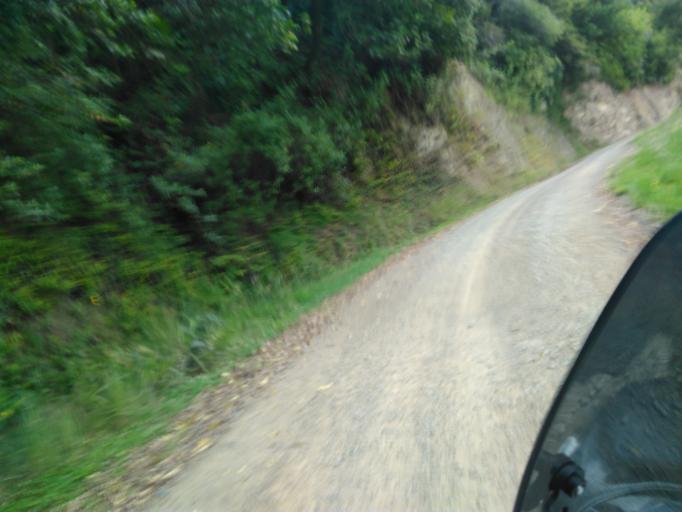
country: NZ
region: Bay of Plenty
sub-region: Opotiki District
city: Opotiki
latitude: -38.0329
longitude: 177.4408
